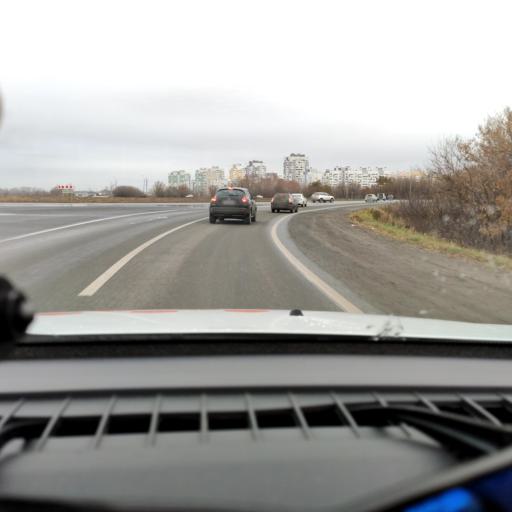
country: RU
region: Samara
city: Samara
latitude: 53.0906
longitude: 50.1496
